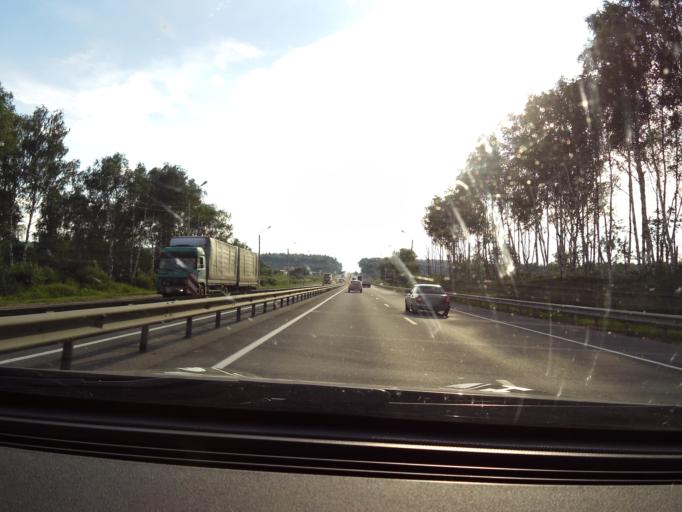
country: RU
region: Vladimir
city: Melekhovo
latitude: 56.2083
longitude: 41.2417
